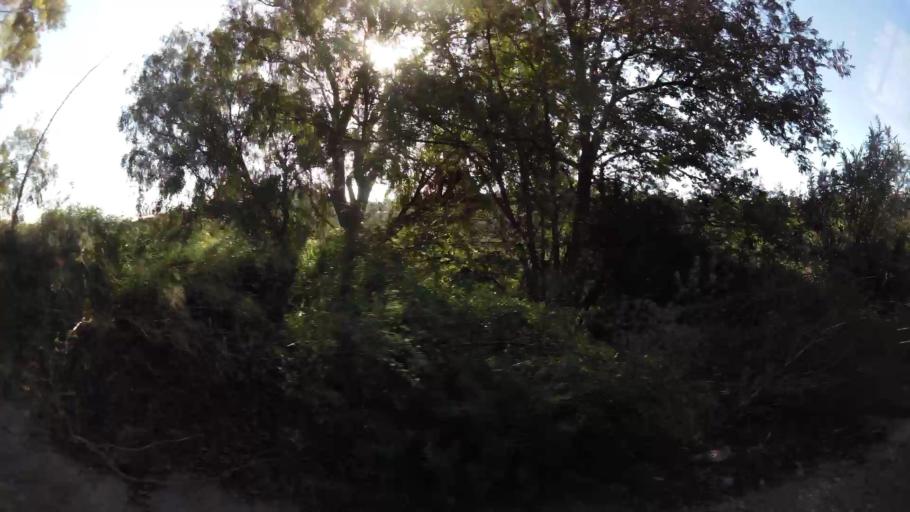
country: GR
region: Attica
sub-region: Nomarchia Anatolikis Attikis
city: Dhrafi
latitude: 38.0224
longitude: 23.9106
